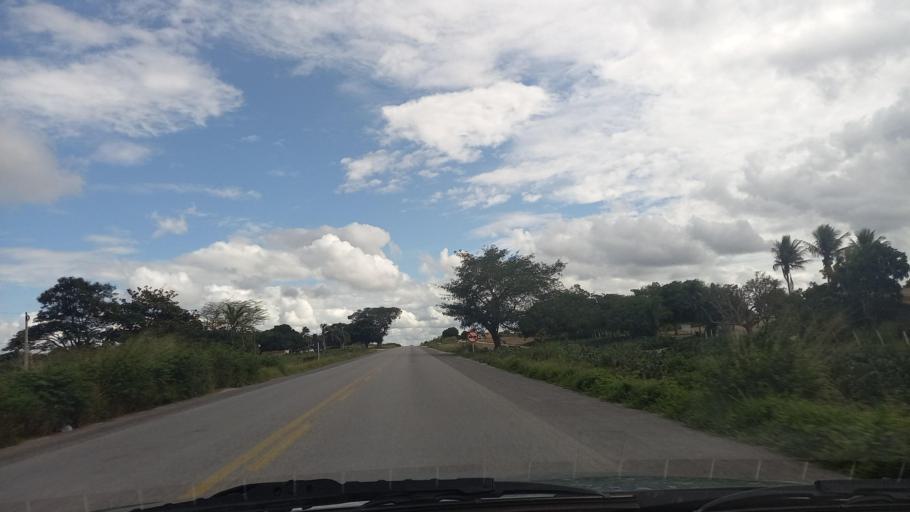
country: BR
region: Pernambuco
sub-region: Lajedo
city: Lajedo
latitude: -8.6803
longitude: -36.4050
